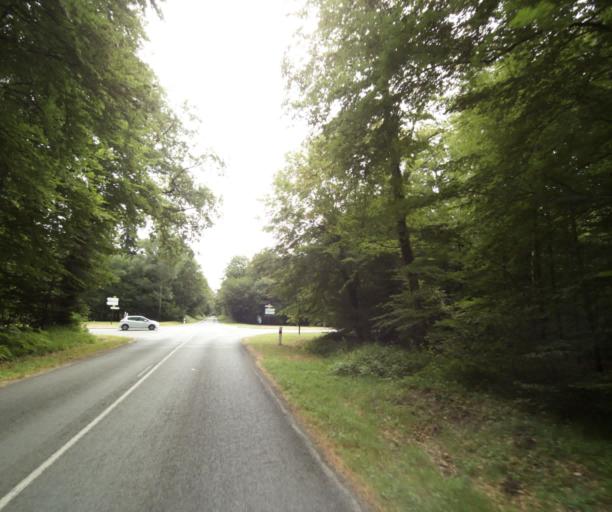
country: FR
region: Ile-de-France
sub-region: Departement de Seine-et-Marne
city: Bois-le-Roi
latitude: 48.4578
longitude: 2.7245
